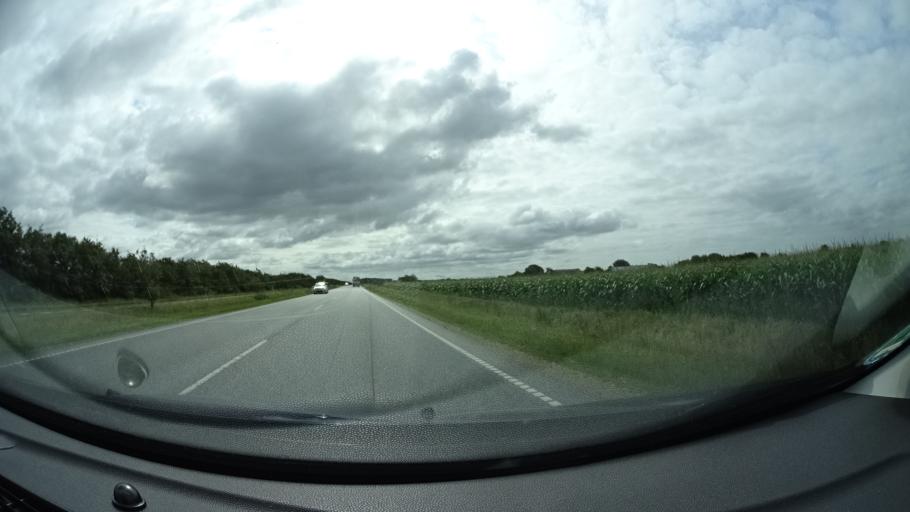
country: DK
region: South Denmark
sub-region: Esbjerg Kommune
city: Ribe
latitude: 55.3791
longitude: 8.7582
